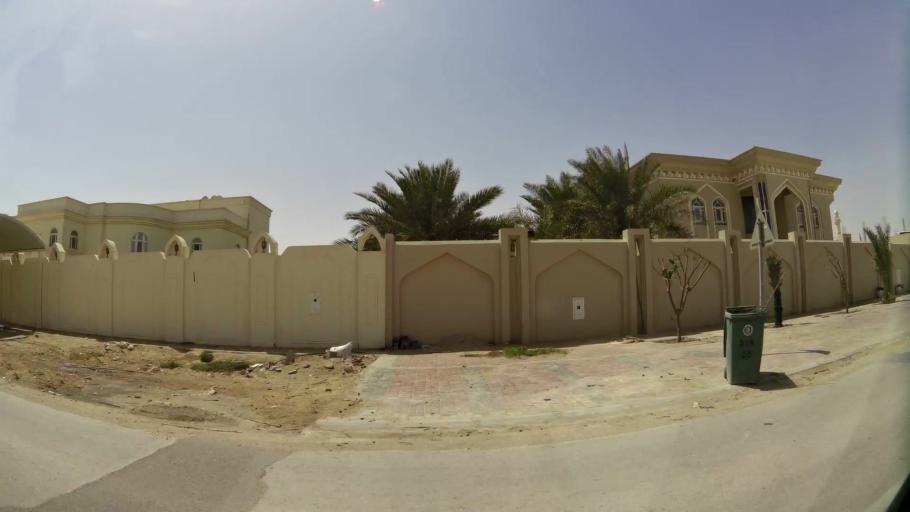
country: QA
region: Baladiyat Umm Salal
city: Umm Salal Muhammad
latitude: 25.3735
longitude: 51.4538
